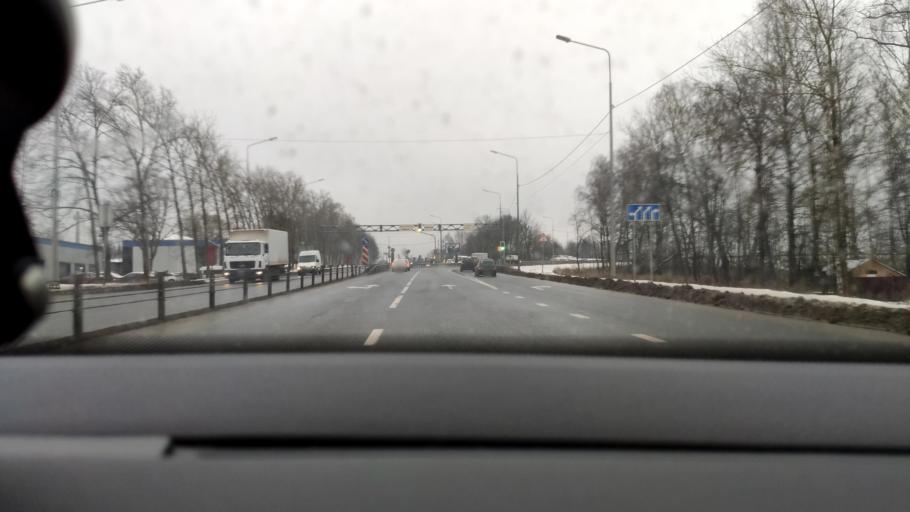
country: RU
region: Moskovskaya
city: Sergiyev Posad
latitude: 56.2777
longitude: 38.1227
